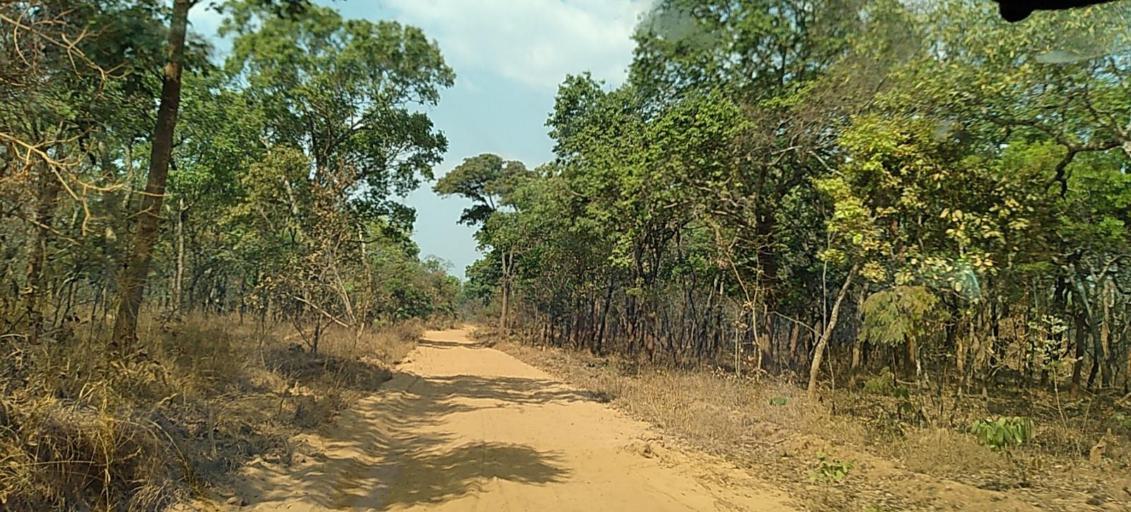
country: ZM
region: North-Western
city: Kasempa
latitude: -13.3207
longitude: 26.0438
